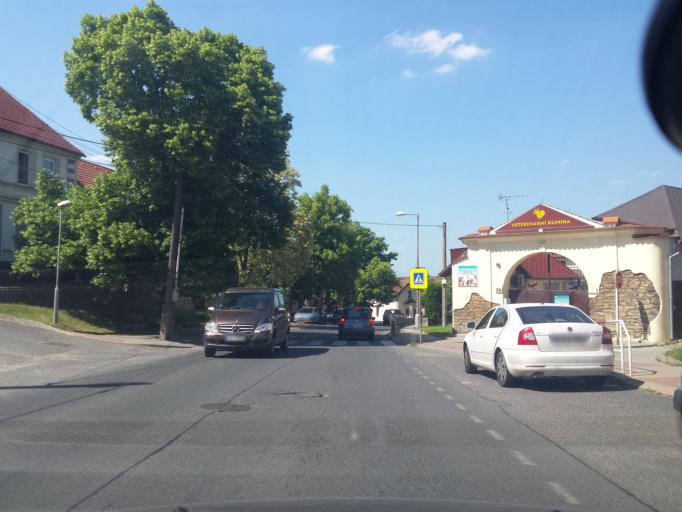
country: CZ
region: Central Bohemia
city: Horomerice
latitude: 50.1335
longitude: 14.3364
